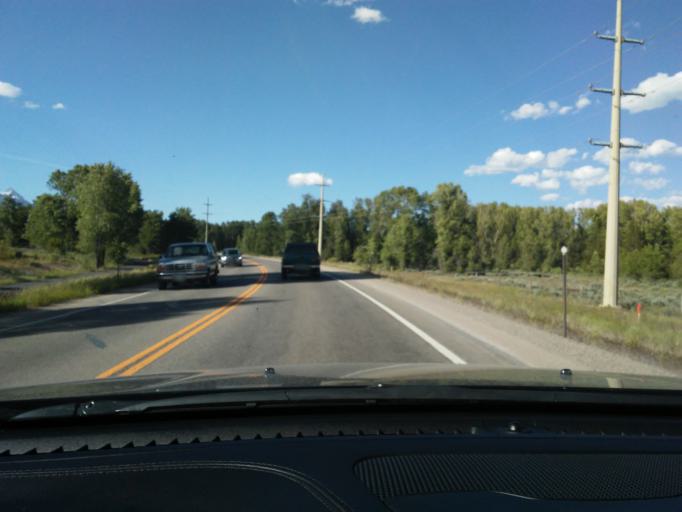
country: US
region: Wyoming
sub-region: Teton County
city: Moose Wilson Road
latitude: 43.5401
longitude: -110.8230
